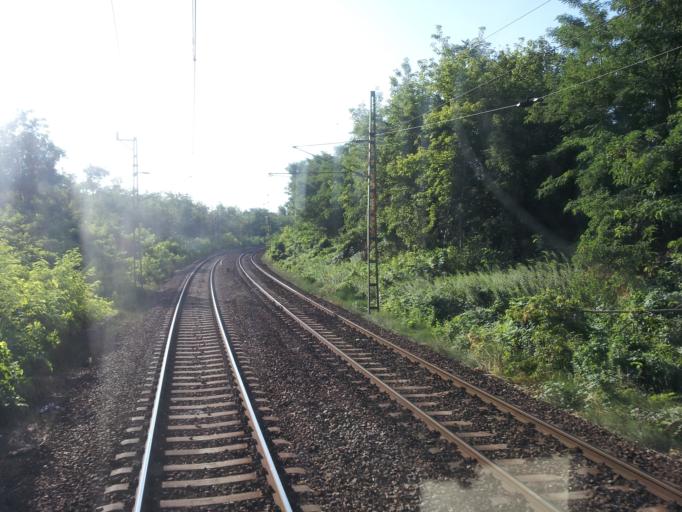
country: HU
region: Budapest
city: Budapest XIV. keruelet
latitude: 47.4883
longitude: 19.1159
